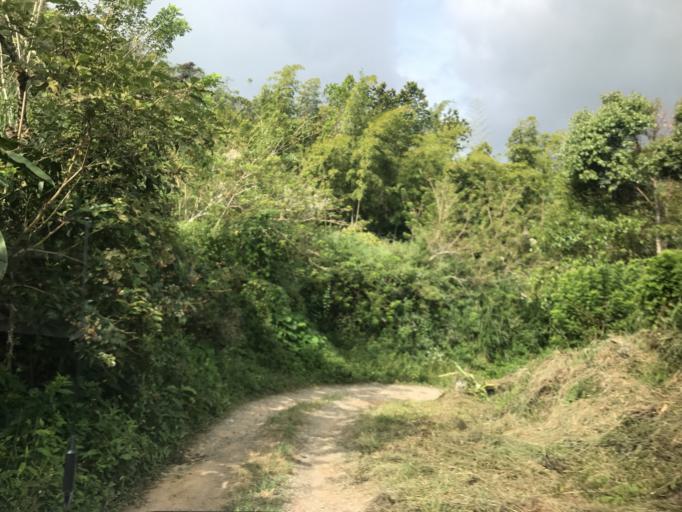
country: CO
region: Valle del Cauca
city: Obando
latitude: 4.5612
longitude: -75.8793
